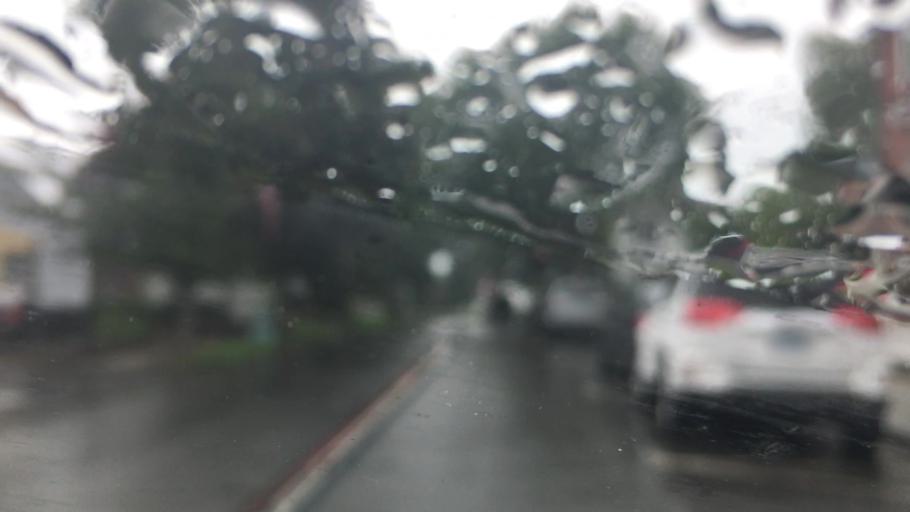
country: US
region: Connecticut
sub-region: Middlesex County
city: Essex Village
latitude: 41.3512
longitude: -72.3863
